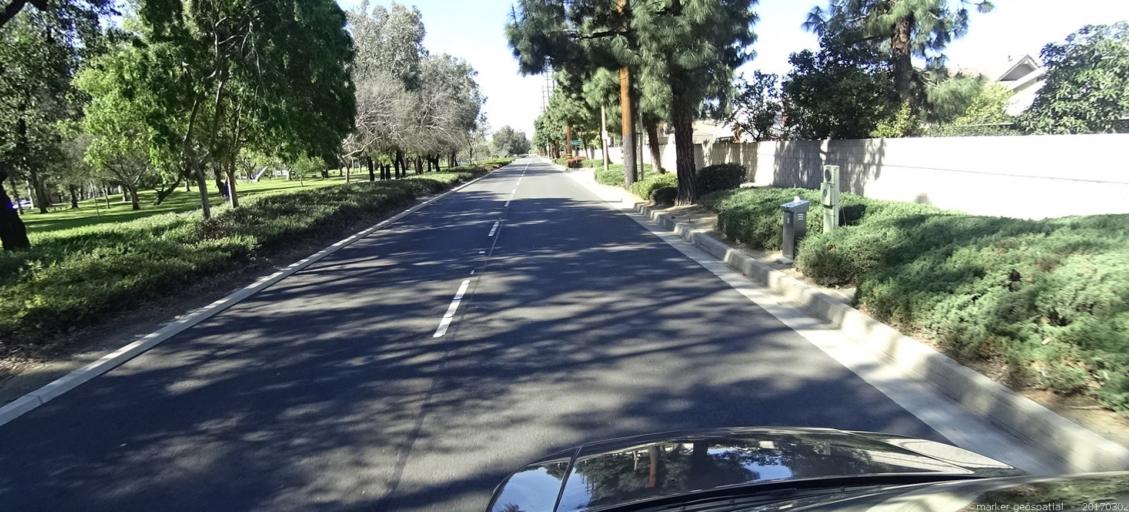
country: US
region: California
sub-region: Orange County
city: Yorba Linda
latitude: 33.8725
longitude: -117.7611
